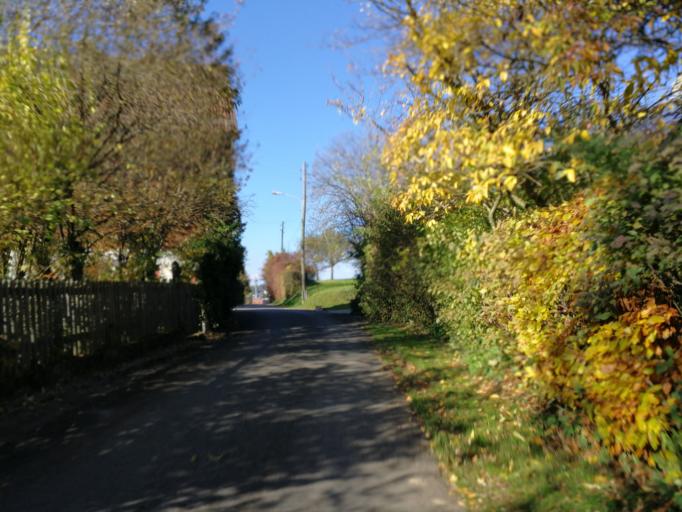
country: CH
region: Zurich
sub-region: Bezirk Uster
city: Esslingen
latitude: 47.2841
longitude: 8.7166
